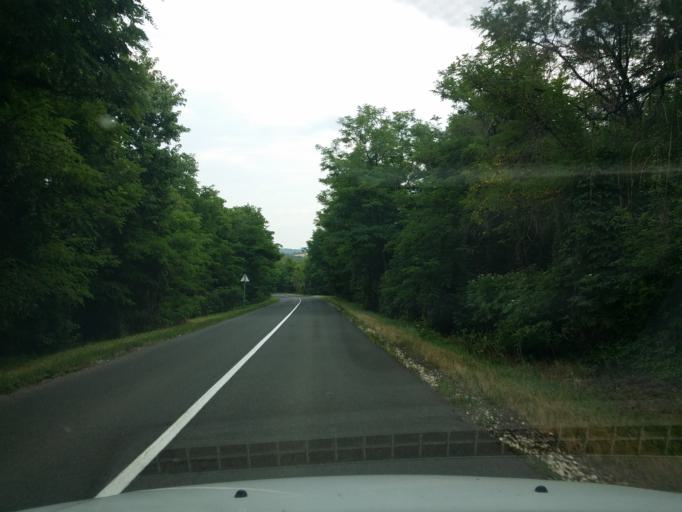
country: HU
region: Nograd
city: Bercel
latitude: 47.9188
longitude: 19.3674
